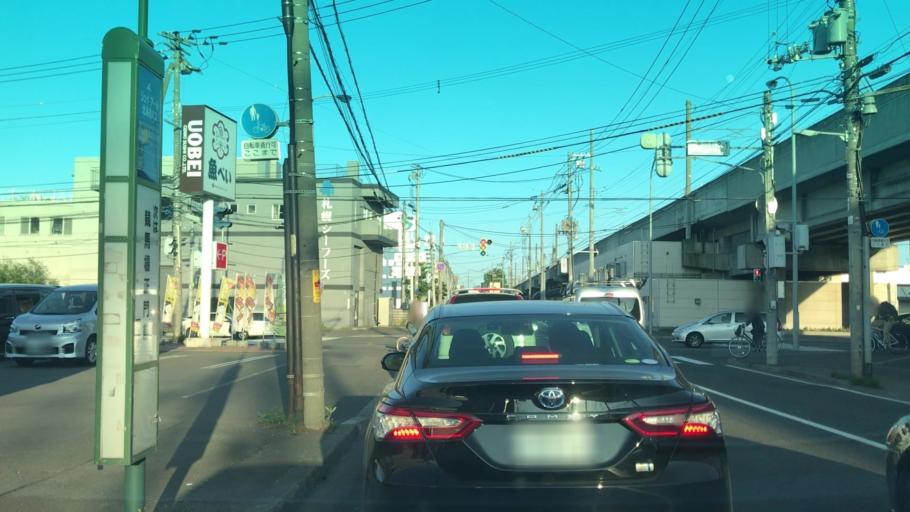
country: JP
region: Hokkaido
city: Sapporo
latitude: 43.0777
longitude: 141.3162
